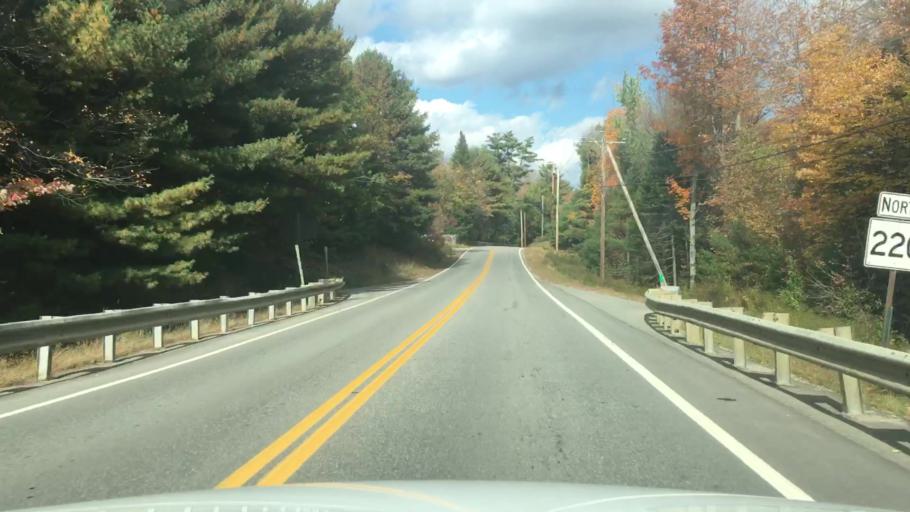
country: US
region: Maine
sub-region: Knox County
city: Washington
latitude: 44.3215
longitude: -69.3606
